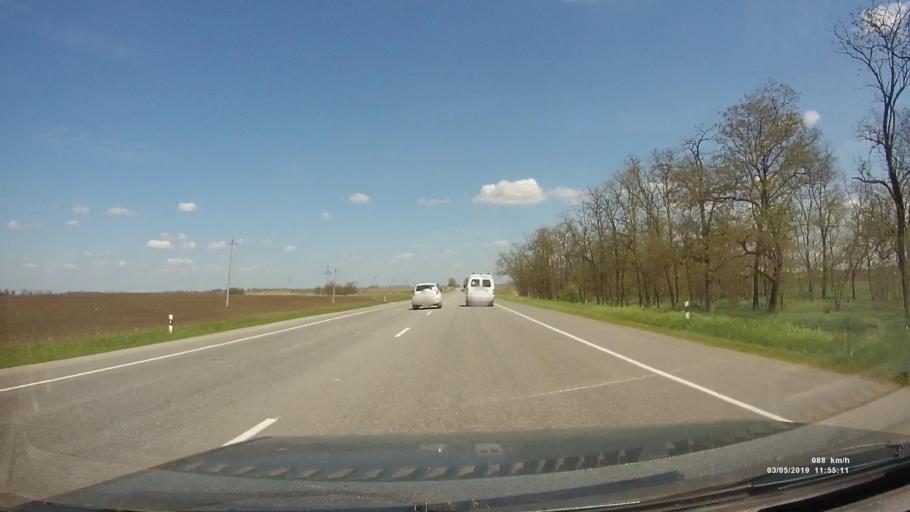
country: RU
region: Rostov
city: Bagayevskaya
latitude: 47.1796
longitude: 40.2884
